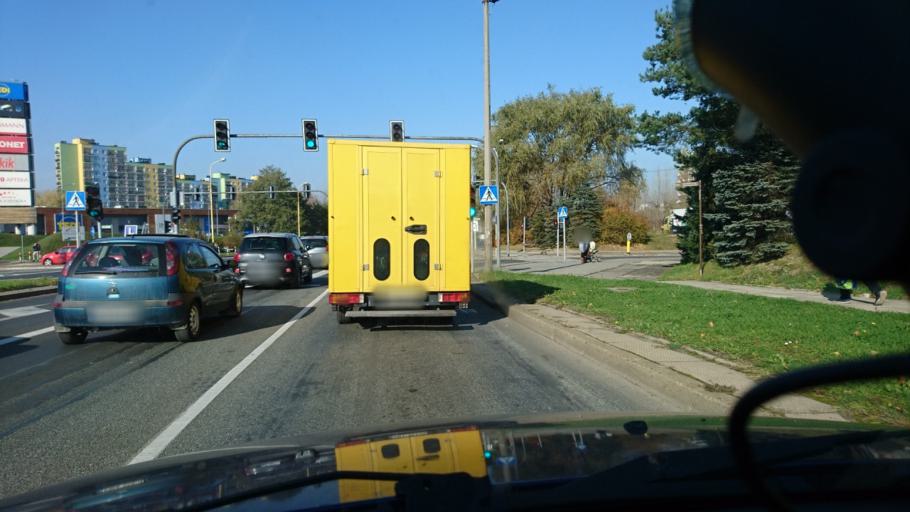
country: PL
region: Silesian Voivodeship
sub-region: Bielsko-Biala
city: Bielsko-Biala
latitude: 49.8016
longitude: 19.0319
